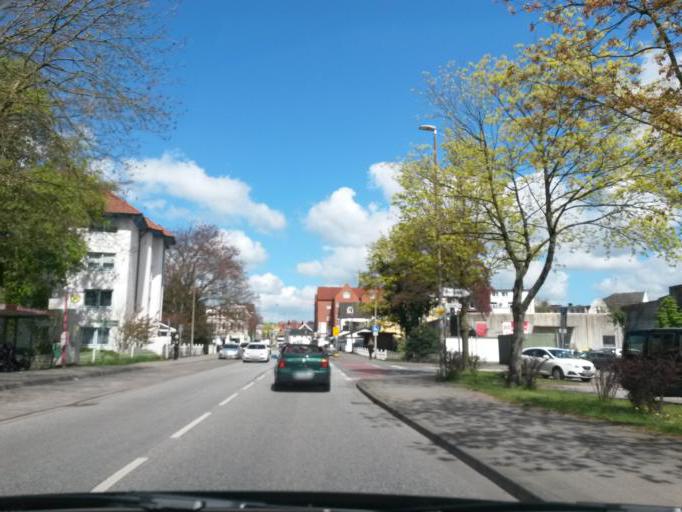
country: DE
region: Schleswig-Holstein
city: Uetersen
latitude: 53.6829
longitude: 9.6633
